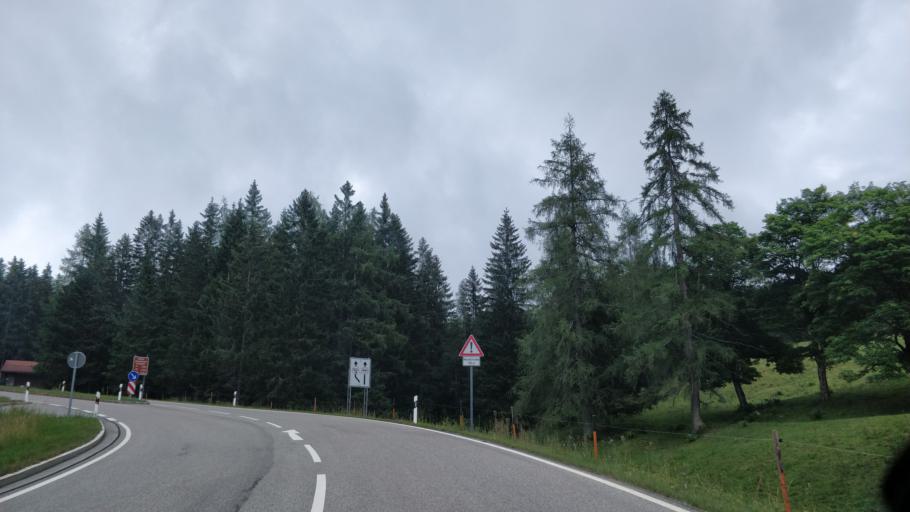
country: AT
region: Salzburg
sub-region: Politischer Bezirk Hallein
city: Hallein
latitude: 47.6411
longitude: 13.0911
